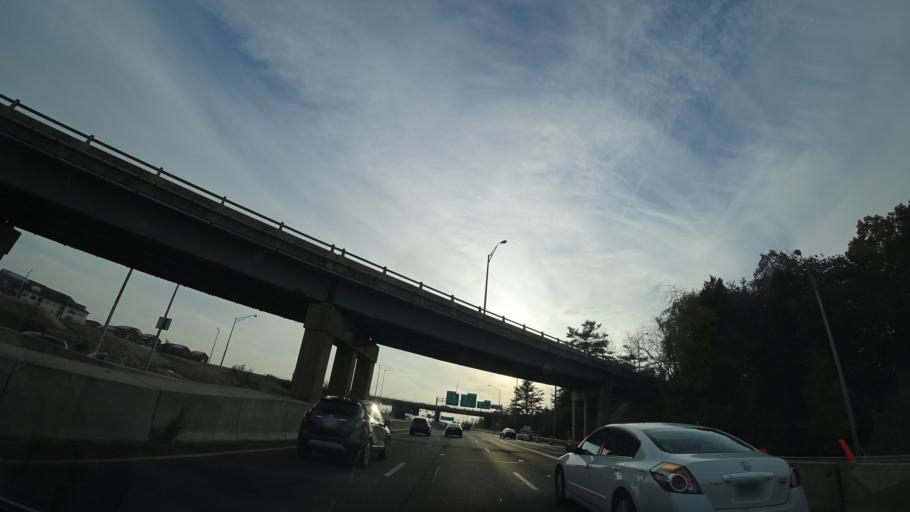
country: US
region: Virginia
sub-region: Fairfax County
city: Lincolnia
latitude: 38.8033
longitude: -77.1626
